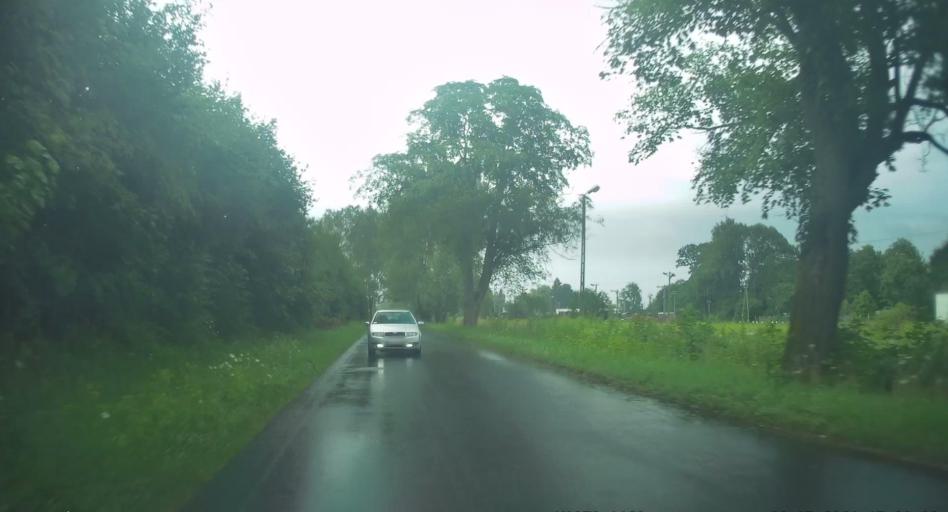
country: PL
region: Lodz Voivodeship
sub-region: Powiat brzezinski
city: Rogow
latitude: 51.8121
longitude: 19.8786
